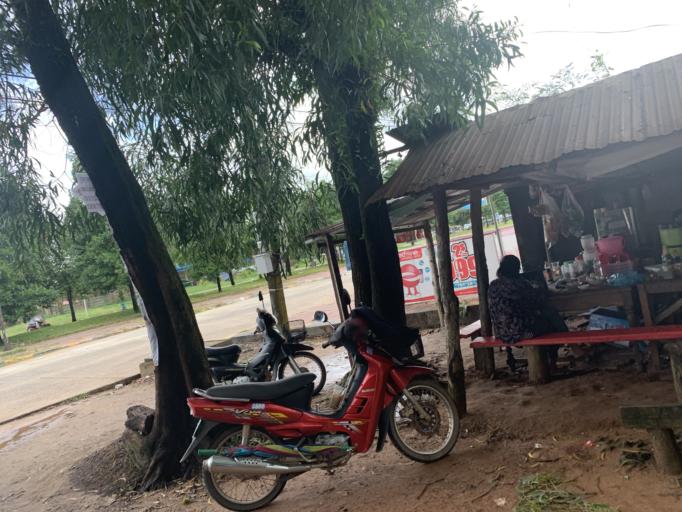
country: KH
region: Koh Kong
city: Koh Kong
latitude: 11.6207
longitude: 102.9820
